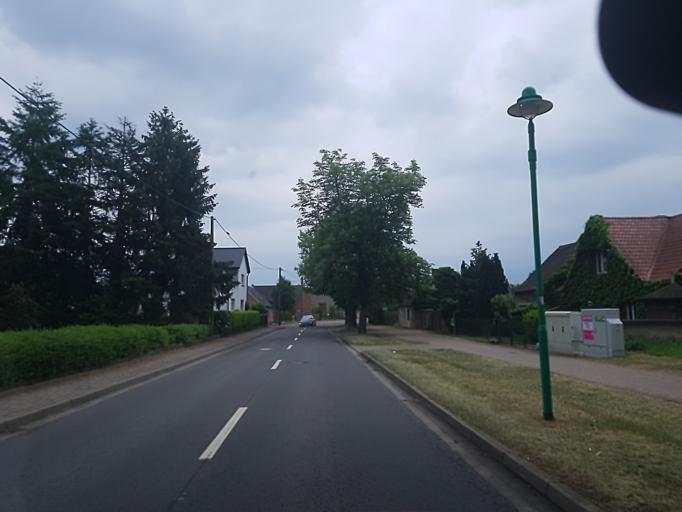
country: DE
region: Saxony-Anhalt
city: Jessen
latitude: 51.7953
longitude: 13.0208
